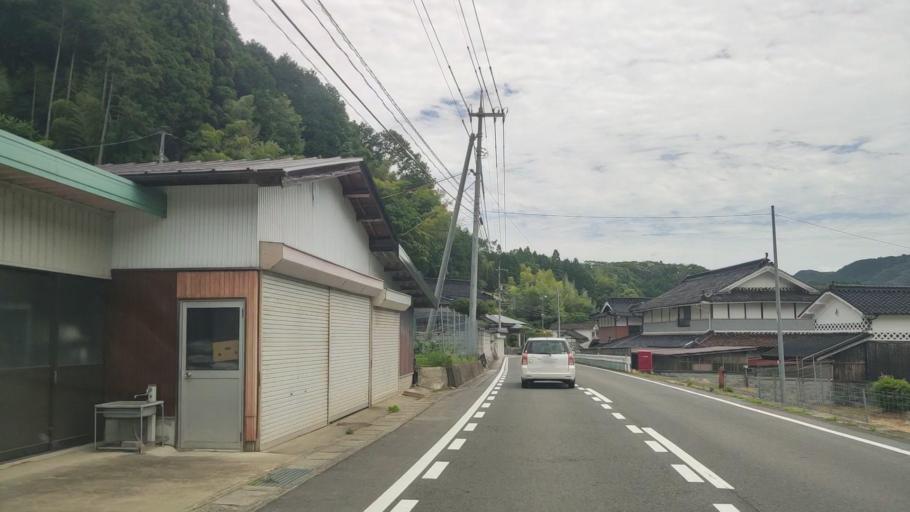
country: JP
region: Hyogo
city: Yamazakicho-nakabirose
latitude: 35.1016
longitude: 134.3137
